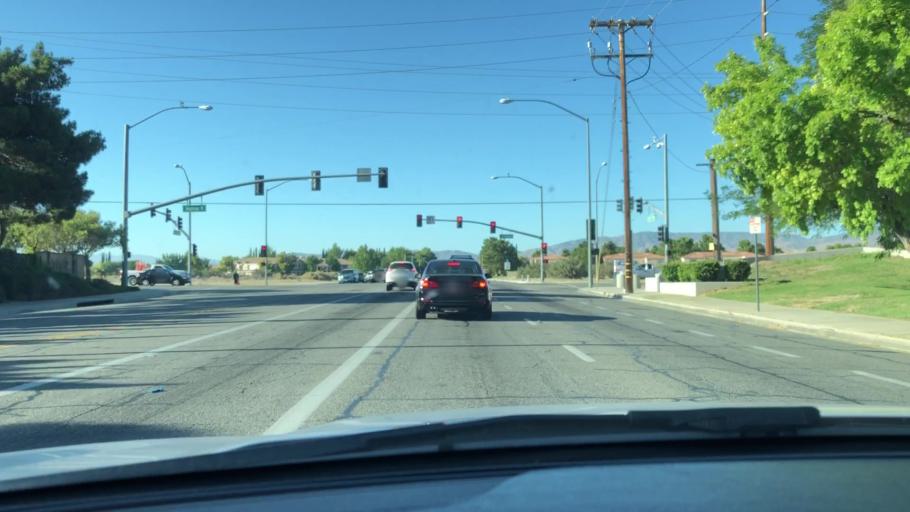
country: US
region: California
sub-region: Los Angeles County
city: Quartz Hill
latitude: 34.6756
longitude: -118.1836
